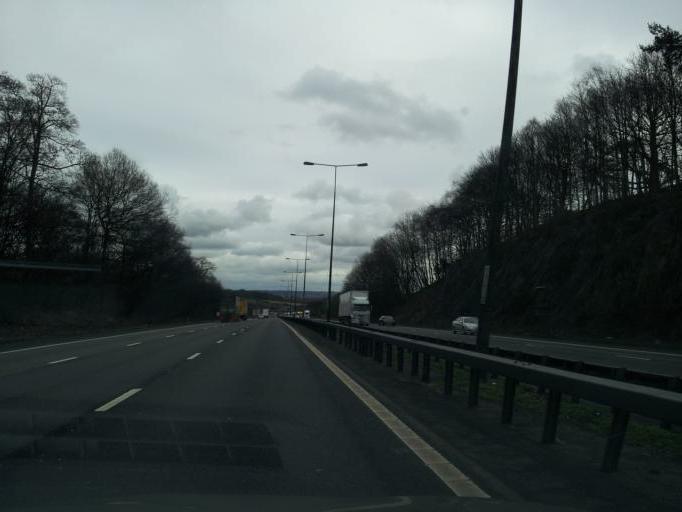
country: GB
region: England
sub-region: Staffordshire
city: Newcastle under Lyme
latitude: 52.9907
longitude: -2.2681
